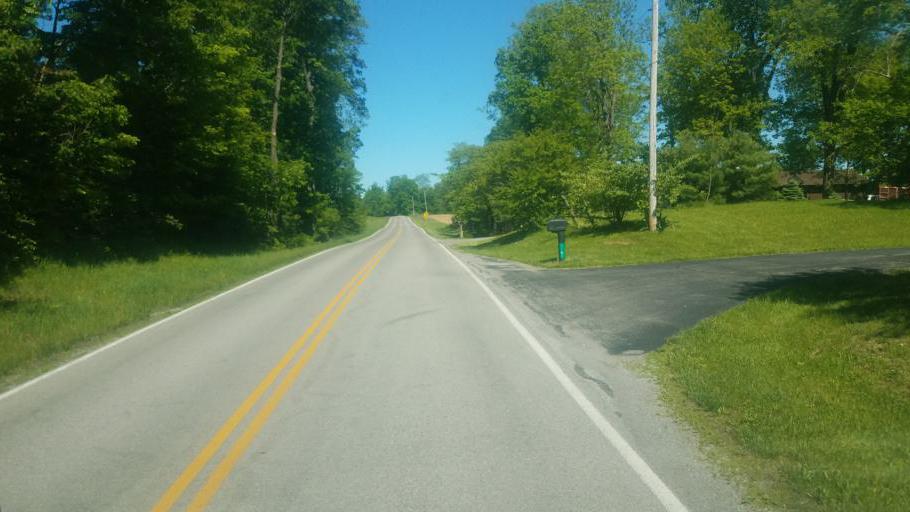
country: US
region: Ohio
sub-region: Logan County
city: Bellefontaine
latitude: 40.4127
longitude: -83.7800
